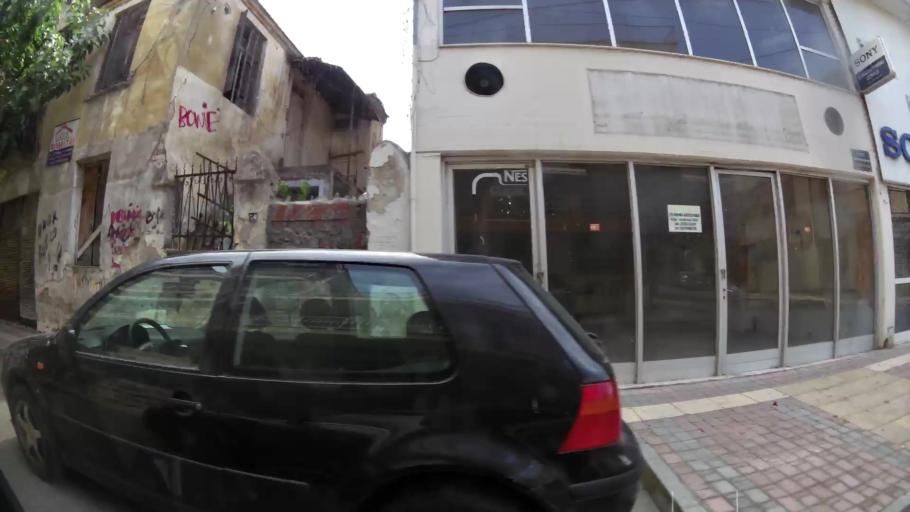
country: GR
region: Central Macedonia
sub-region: Nomos Pierias
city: Katerini
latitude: 40.2734
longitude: 22.5038
